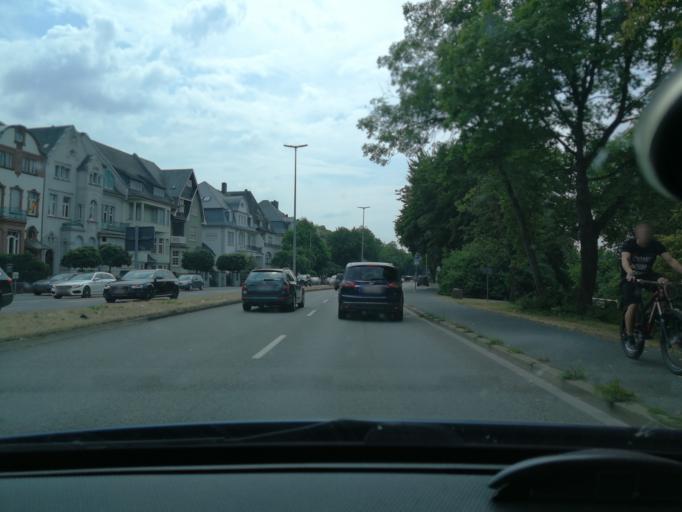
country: DE
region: Rheinland-Pfalz
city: Trier
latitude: 49.7619
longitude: 6.6330
